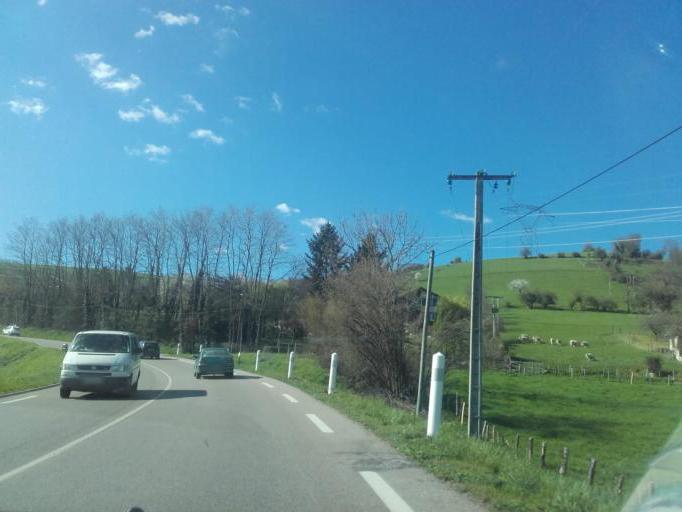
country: FR
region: Rhone-Alpes
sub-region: Departement de l'Isere
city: Saint-Hilaire-de-la-Cote
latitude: 45.3991
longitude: 5.3570
